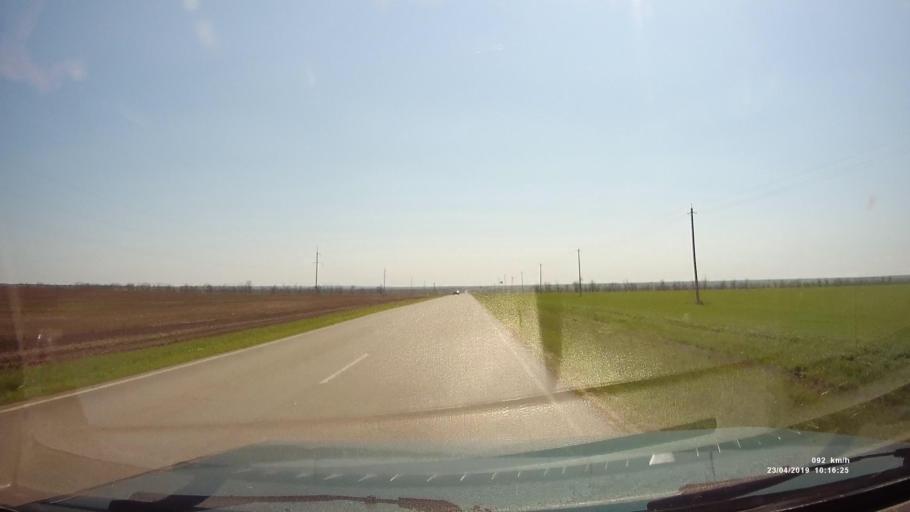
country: RU
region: Rostov
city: Sovetskoye
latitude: 46.6586
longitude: 42.3953
